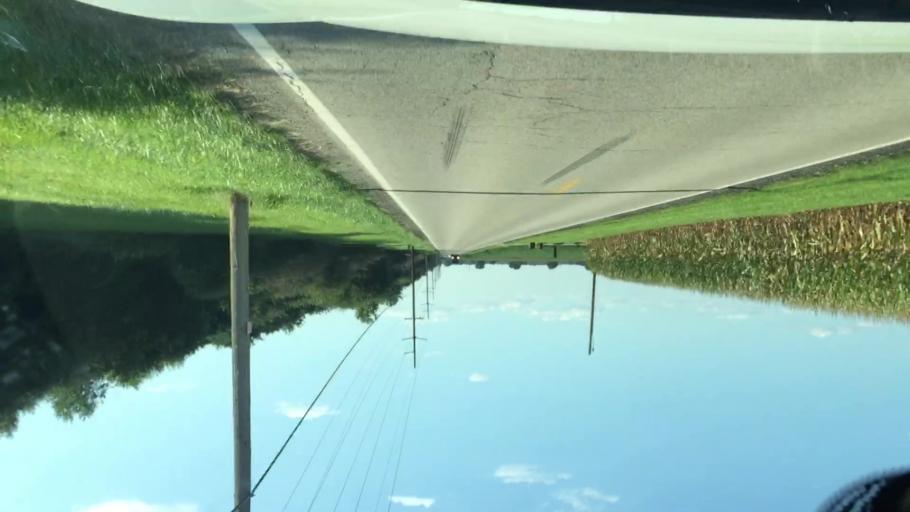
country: US
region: Ohio
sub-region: Clark County
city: Northridge
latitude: 39.9600
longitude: -83.7083
